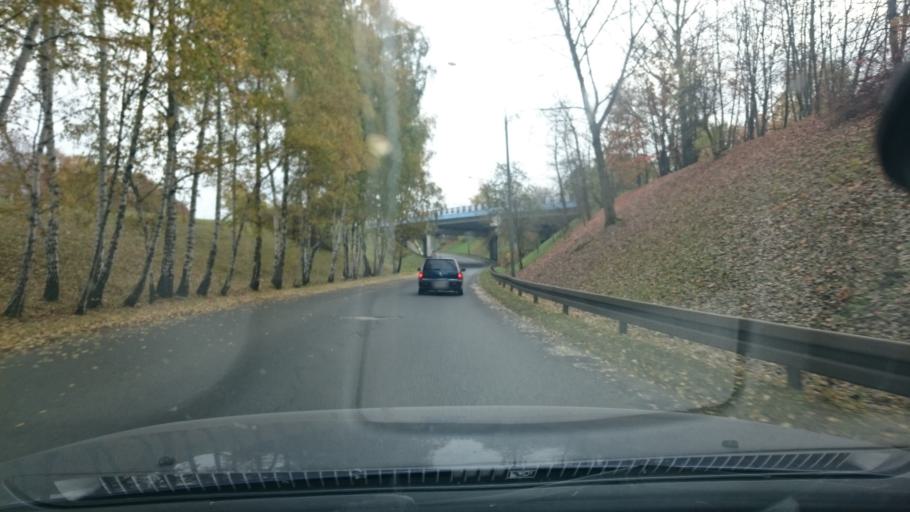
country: PL
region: Silesian Voivodeship
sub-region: Sosnowiec
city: Sosnowiec
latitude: 50.3003
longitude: 19.1234
